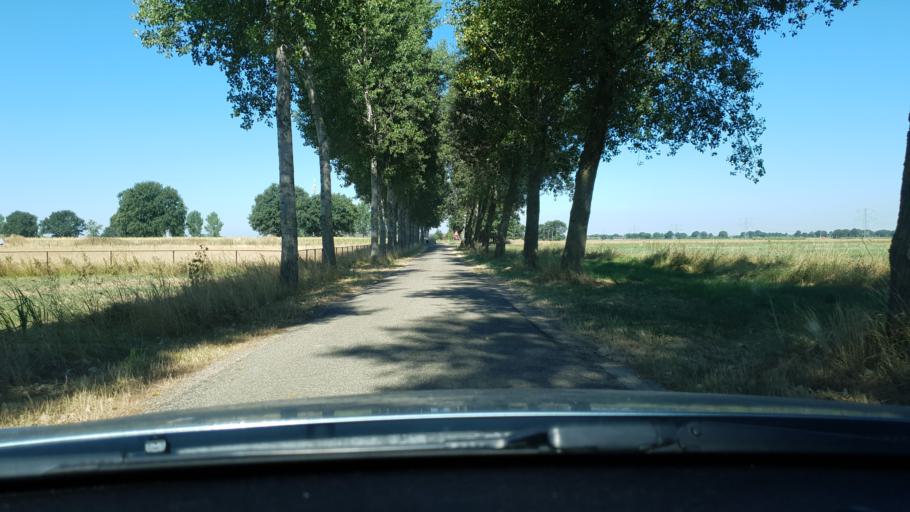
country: NL
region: North Brabant
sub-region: Gemeente Grave
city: Grave
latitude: 51.7756
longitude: 5.7611
